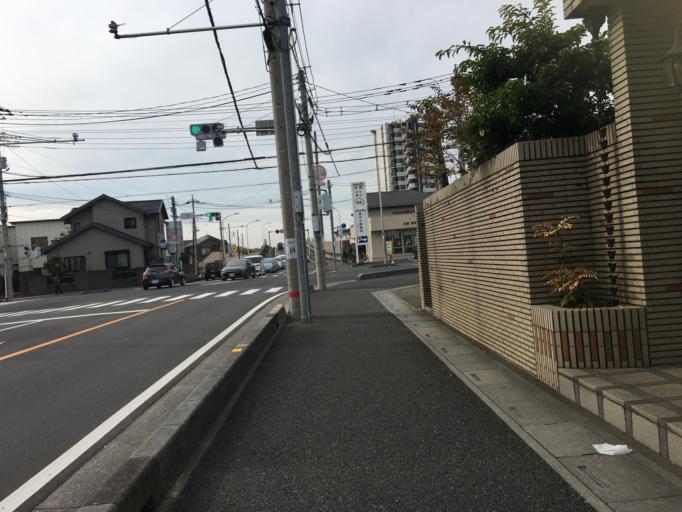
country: JP
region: Saitama
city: Yoshikawa
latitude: 35.8811
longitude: 139.8421
